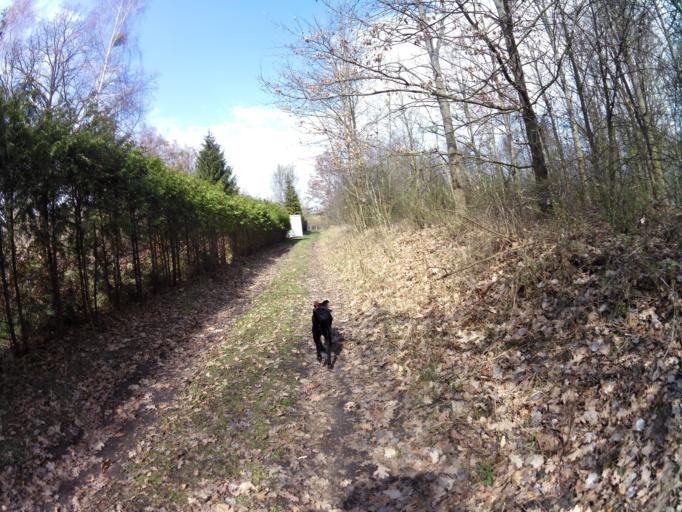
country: PL
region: West Pomeranian Voivodeship
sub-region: Powiat mysliborski
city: Mysliborz
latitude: 52.9401
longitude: 14.8612
